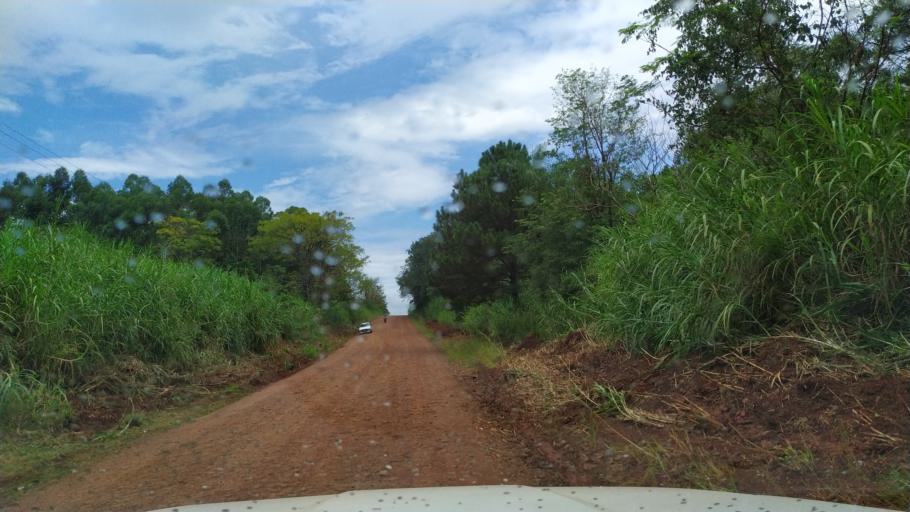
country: AR
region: Misiones
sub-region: Departamento de Eldorado
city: Eldorado
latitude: -26.4242
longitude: -54.6048
